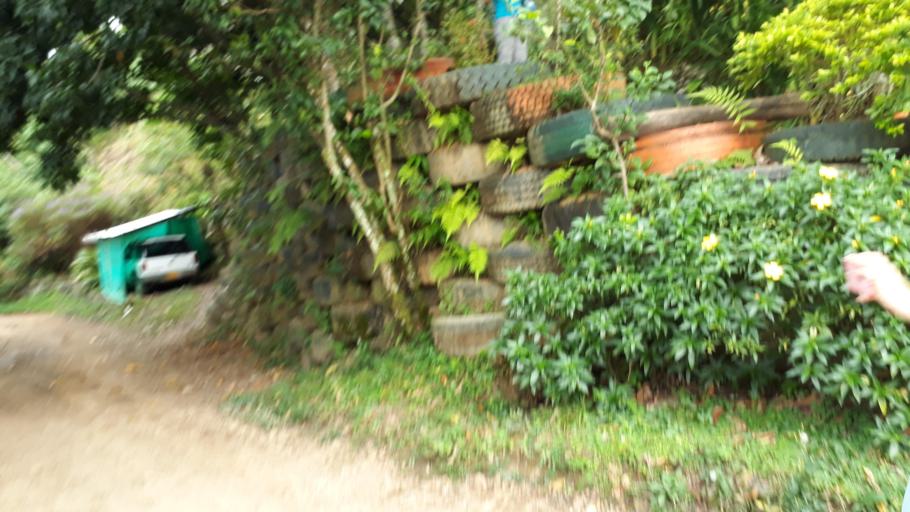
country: CO
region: Valle del Cauca
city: Jamundi
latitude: 3.2067
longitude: -76.6323
